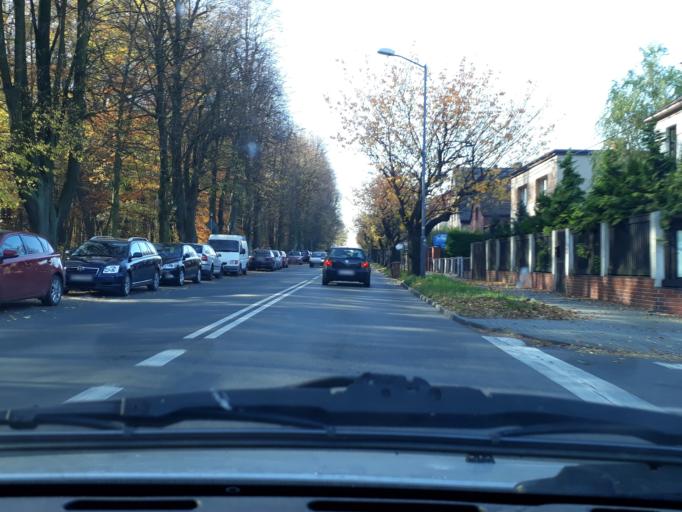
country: PL
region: Silesian Voivodeship
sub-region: Powiat tarnogorski
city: Tarnowskie Gory
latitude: 50.4423
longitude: 18.8439
